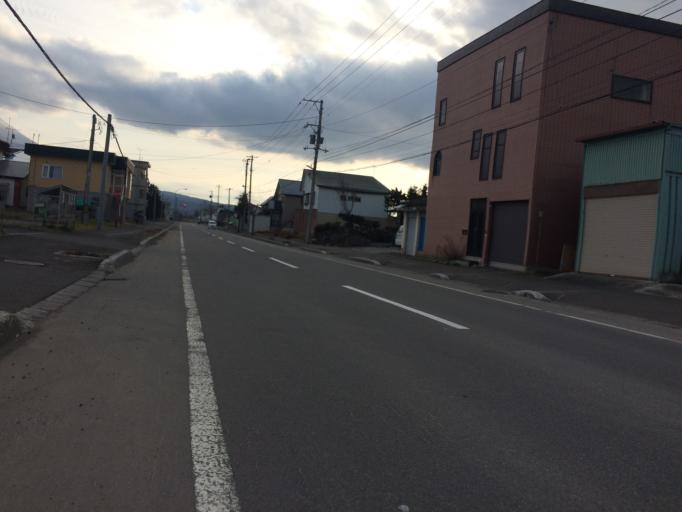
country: JP
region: Hokkaido
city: Niseko Town
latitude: 42.9026
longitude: 140.7665
